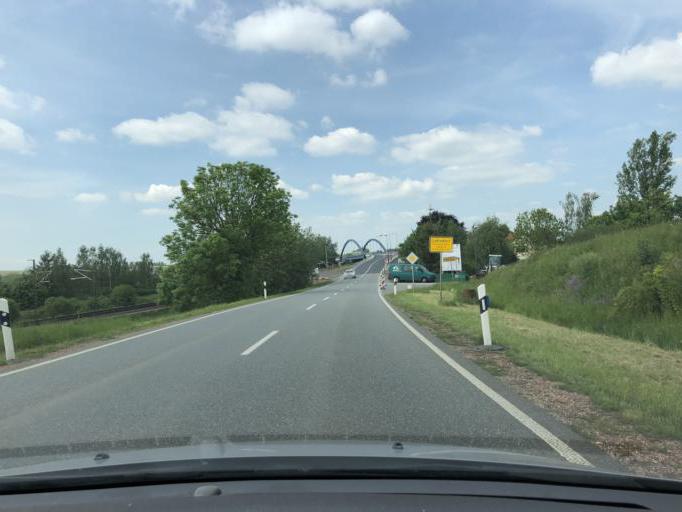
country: DE
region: Thuringia
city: Saara
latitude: 50.9328
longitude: 12.4298
